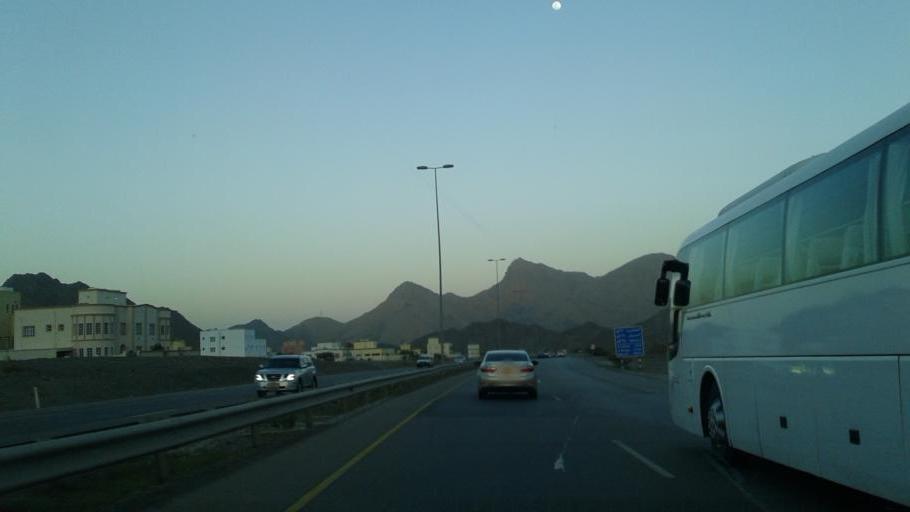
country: OM
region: Muhafazat ad Dakhiliyah
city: Bidbid
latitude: 23.4595
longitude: 58.1763
